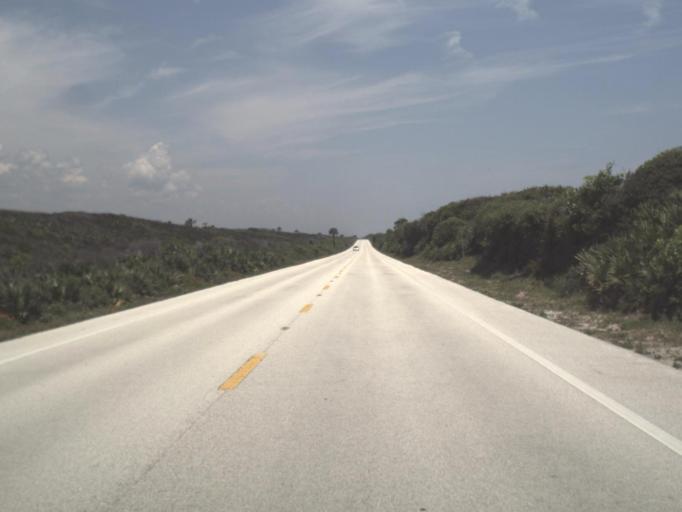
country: US
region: Florida
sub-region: Saint Johns County
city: Palm Valley
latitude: 30.1019
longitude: -81.3420
